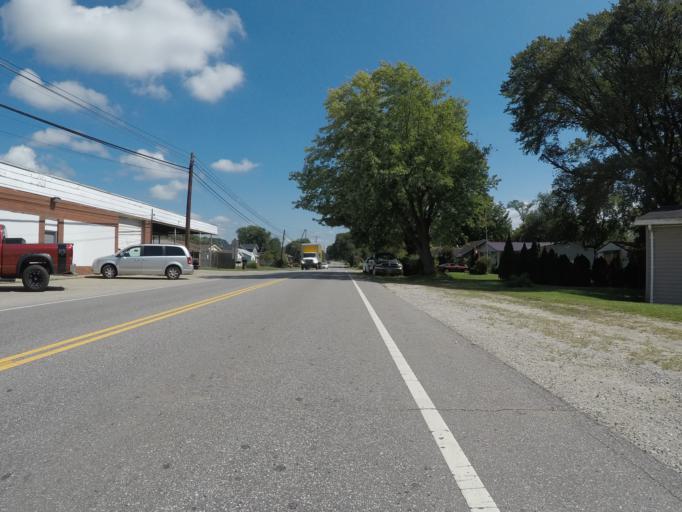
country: US
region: West Virginia
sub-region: Cabell County
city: Huntington
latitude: 38.4226
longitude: -82.4822
